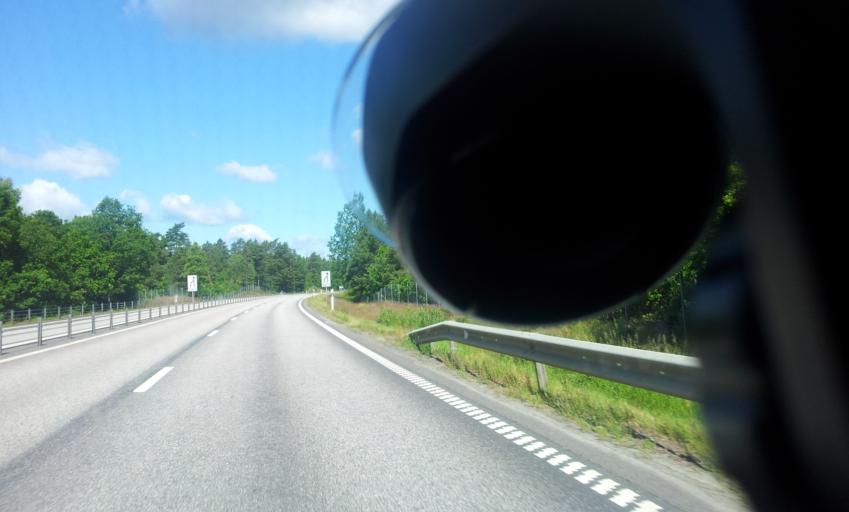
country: SE
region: Kalmar
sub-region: Oskarshamns Kommun
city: Paskallavik
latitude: 57.1578
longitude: 16.4518
